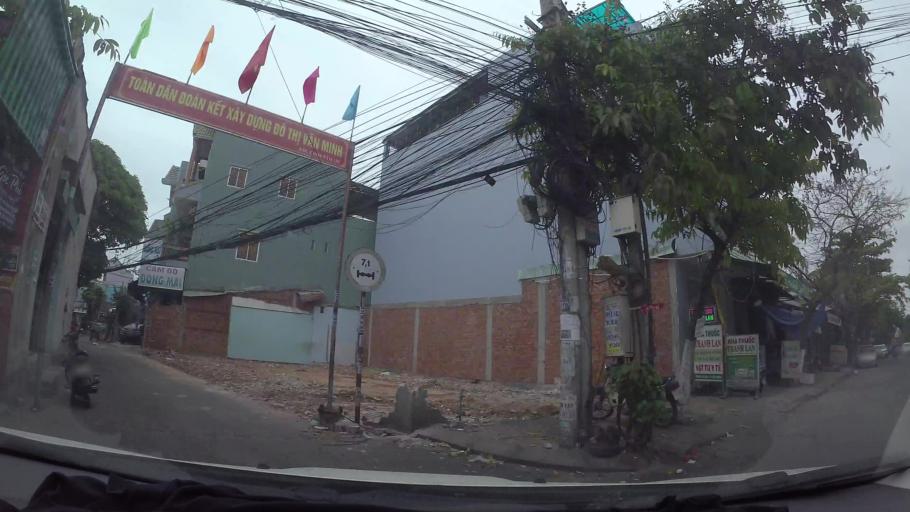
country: VN
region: Da Nang
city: Lien Chieu
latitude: 16.0643
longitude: 108.1525
